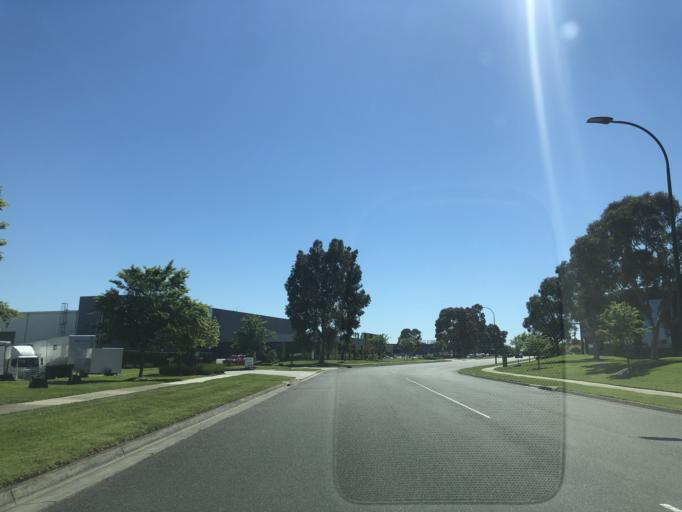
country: AU
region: Victoria
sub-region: Knox
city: Scoresby
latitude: -37.9045
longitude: 145.2179
